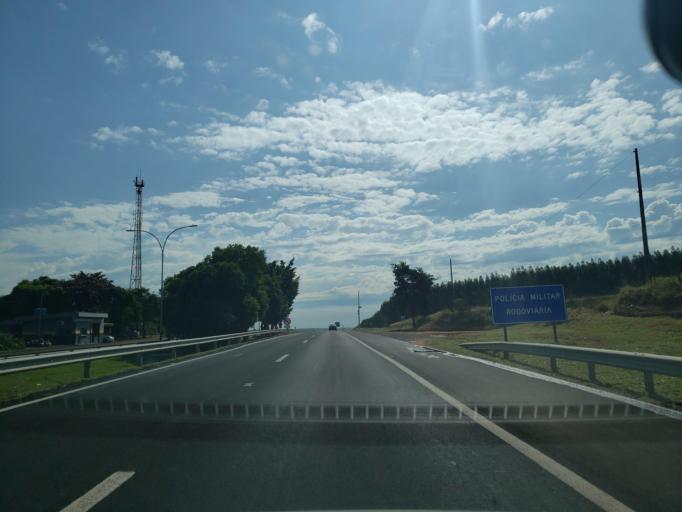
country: BR
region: Sao Paulo
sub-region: Pirajui
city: Pirajui
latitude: -21.9994
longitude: -49.4320
